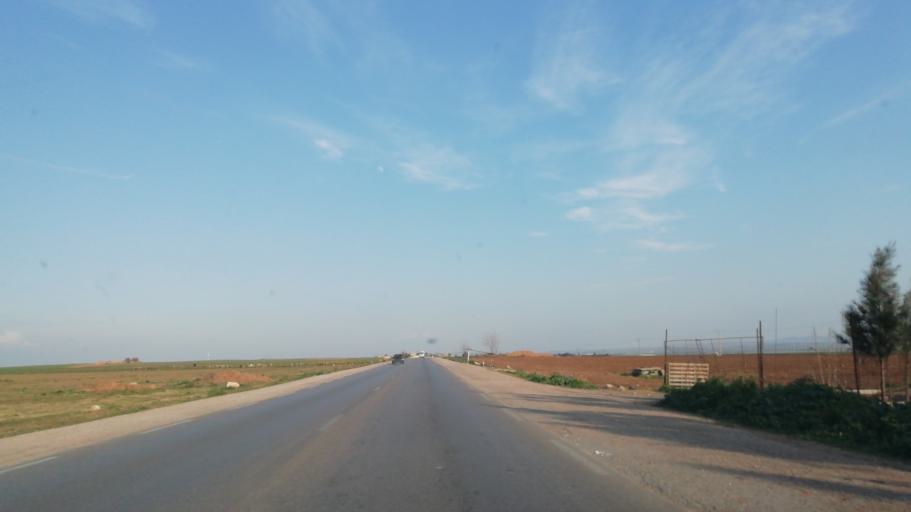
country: DZ
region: Relizane
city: Relizane
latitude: 35.8939
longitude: 0.6468
